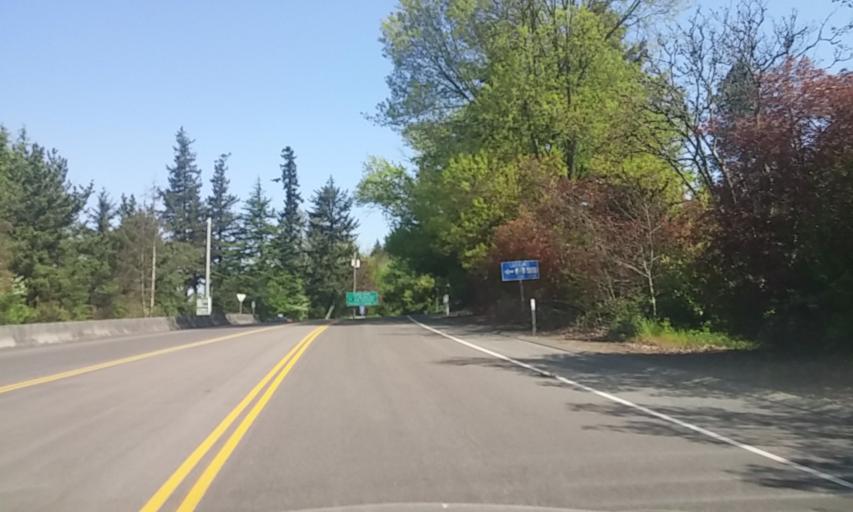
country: US
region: Oregon
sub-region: Washington County
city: Metzger
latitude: 45.4361
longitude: -122.7433
